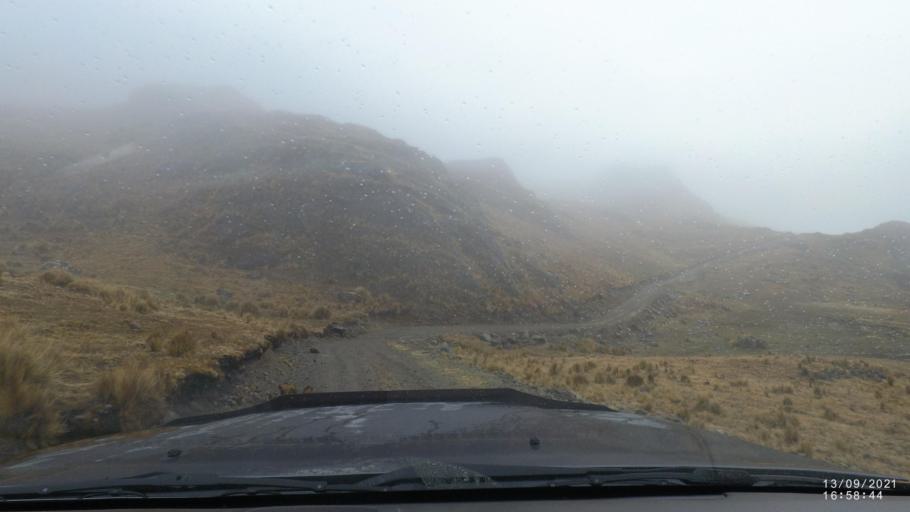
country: BO
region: Cochabamba
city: Colomi
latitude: -17.3090
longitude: -65.7143
